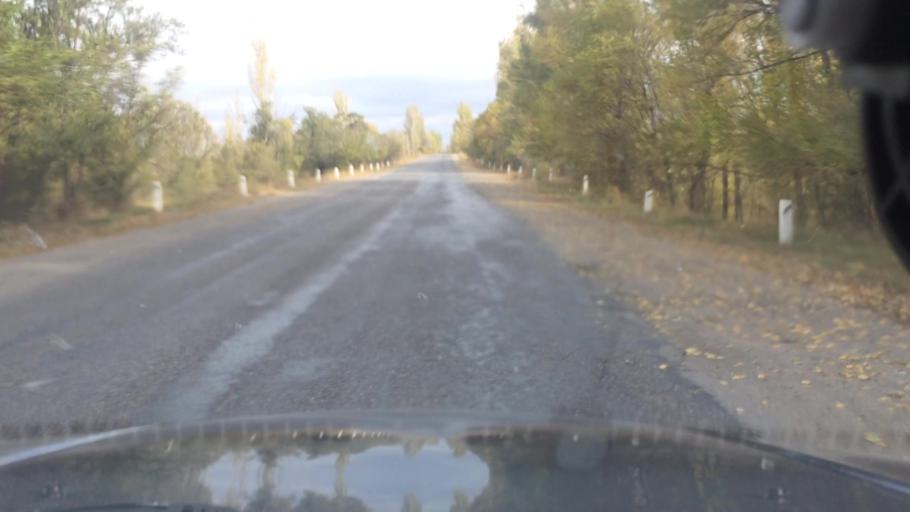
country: KG
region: Ysyk-Koel
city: Karakol
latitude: 42.5665
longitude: 78.3912
